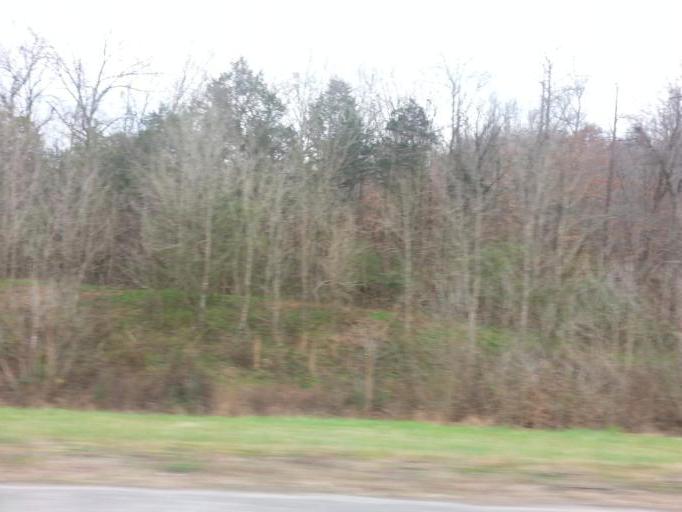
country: US
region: Tennessee
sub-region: Rhea County
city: Graysville
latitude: 35.4195
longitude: -85.0947
